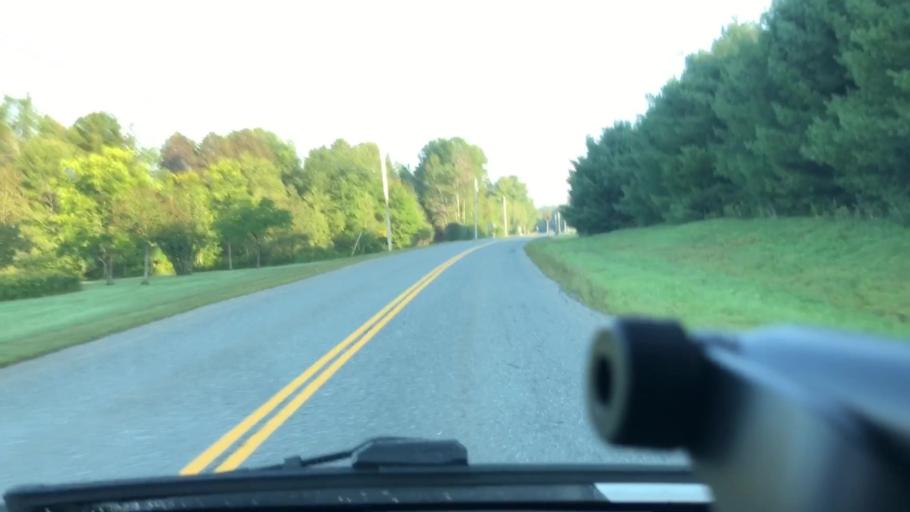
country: US
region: Massachusetts
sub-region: Franklin County
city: Ashfield
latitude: 42.5049
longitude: -72.8806
